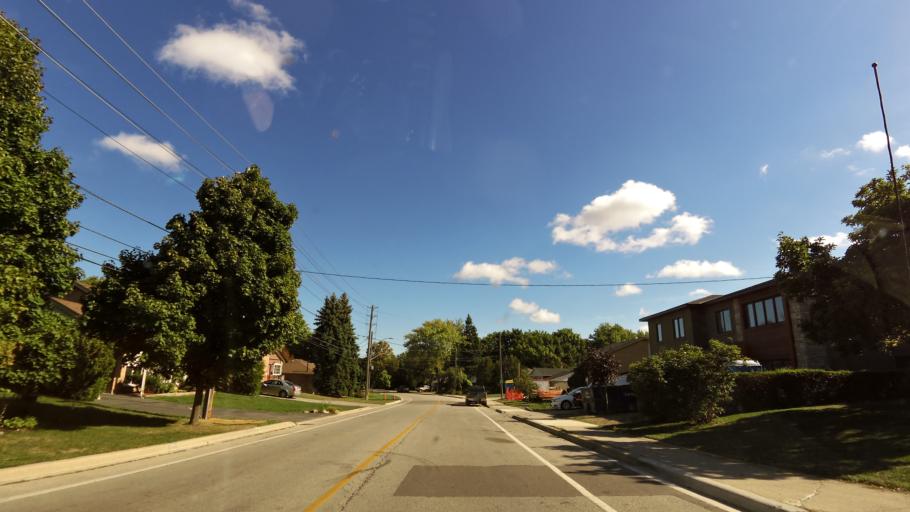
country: CA
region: Ontario
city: Mississauga
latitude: 43.5830
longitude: -79.7240
